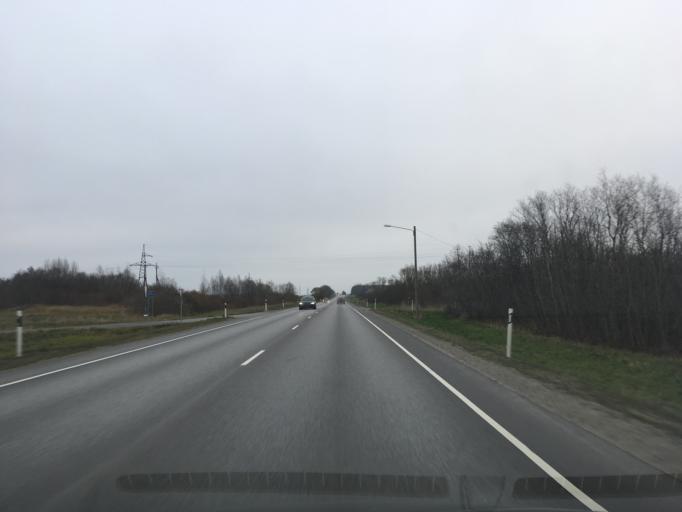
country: EE
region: Ida-Virumaa
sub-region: Kohtla-Jaerve linn
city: Kohtla-Jarve
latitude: 59.4144
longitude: 27.2986
